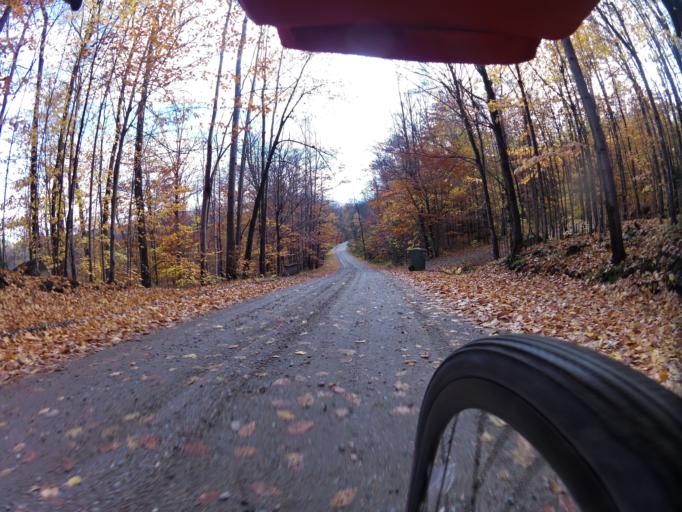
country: CA
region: Quebec
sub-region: Outaouais
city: Wakefield
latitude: 45.7386
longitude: -76.0312
